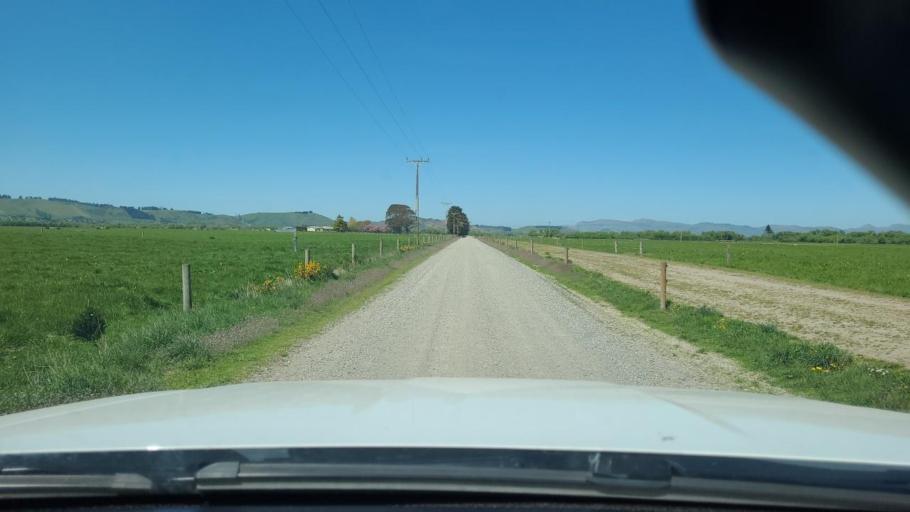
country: NZ
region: Southland
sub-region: Gore District
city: Gore
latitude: -45.8678
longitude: 168.7821
